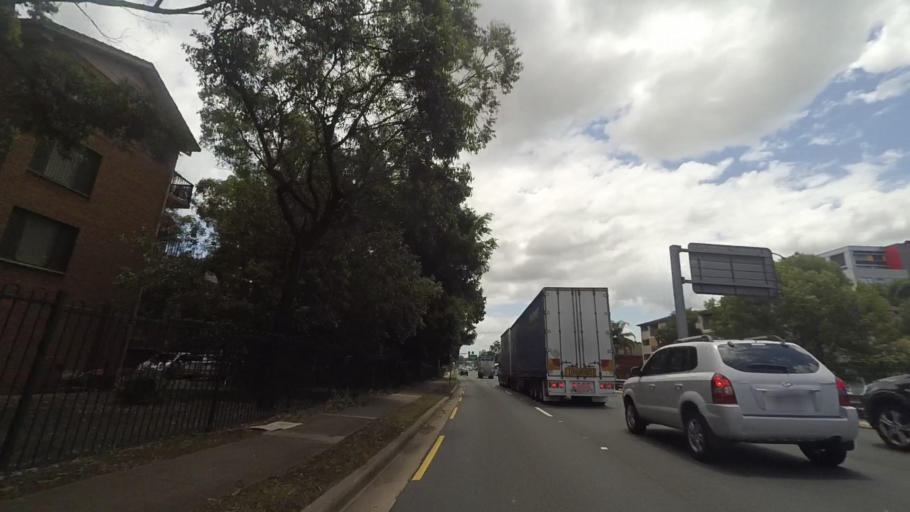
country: AU
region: New South Wales
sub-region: Fairfield
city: Liverpool
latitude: -33.9231
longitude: 150.9186
